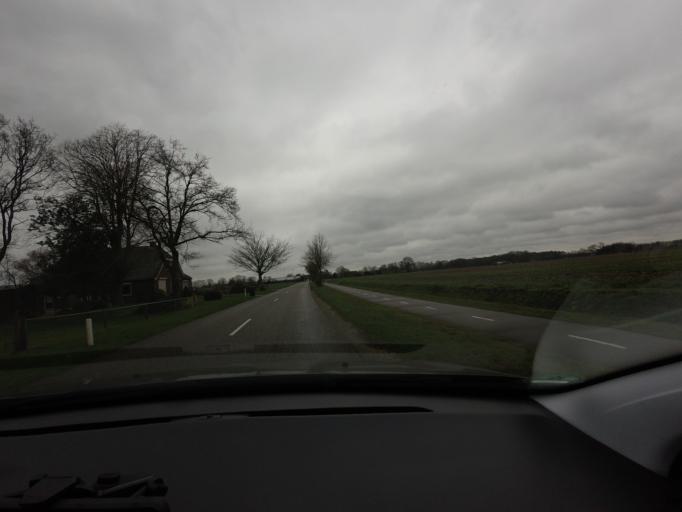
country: NL
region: Drenthe
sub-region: Gemeente Hoogeveen
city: Hoogeveen
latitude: 52.8262
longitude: 6.5185
